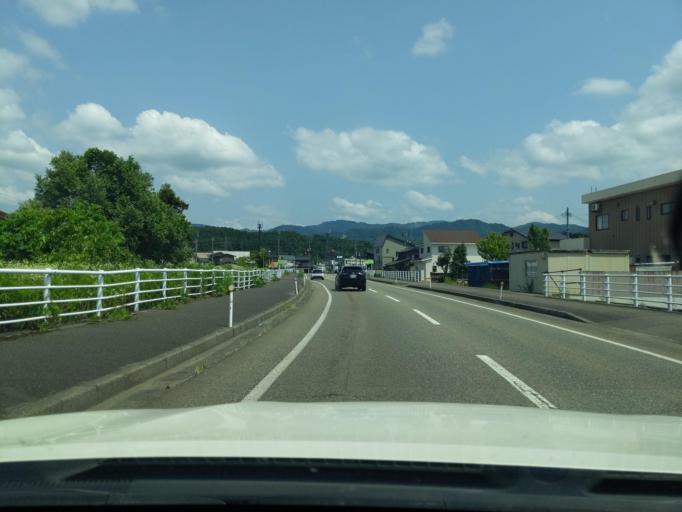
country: JP
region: Niigata
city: Nagaoka
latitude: 37.4270
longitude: 138.8603
